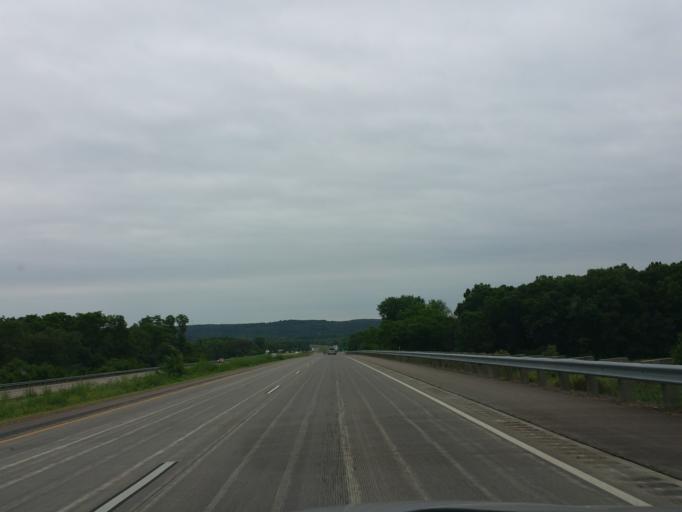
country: US
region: Wisconsin
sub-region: Eau Claire County
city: Eau Claire
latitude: 44.7967
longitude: -91.5522
